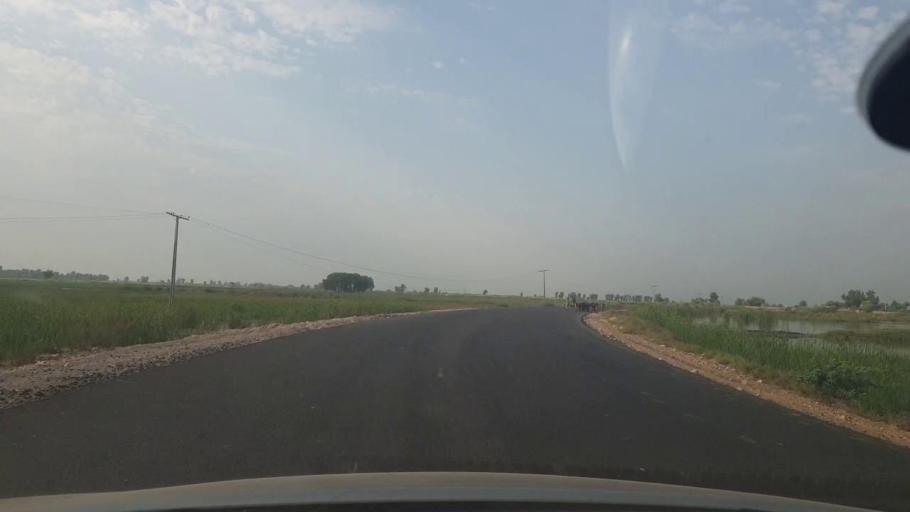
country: PK
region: Sindh
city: Jacobabad
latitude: 28.0959
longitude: 68.3300
